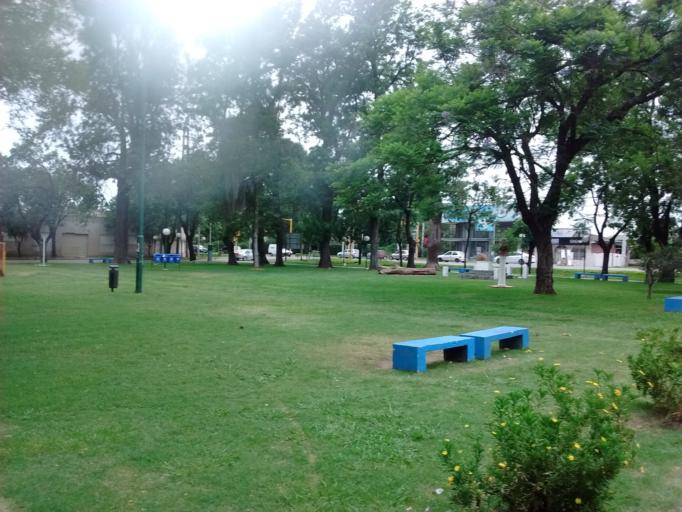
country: AR
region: Santa Fe
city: Funes
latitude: -32.9209
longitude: -60.8116
